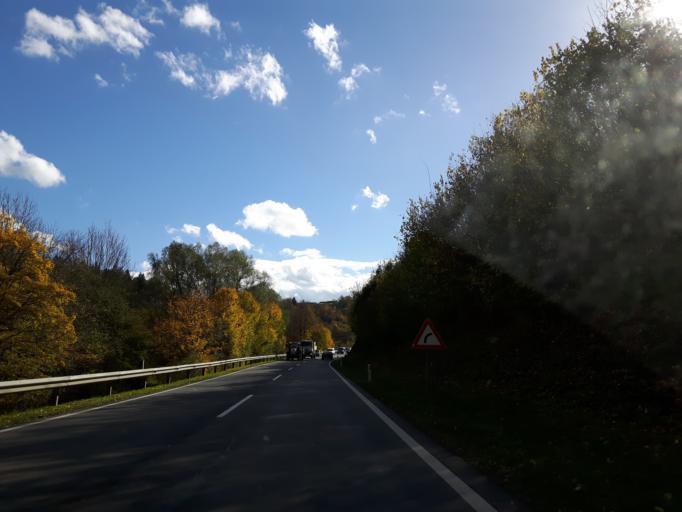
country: AT
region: Styria
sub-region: Politischer Bezirk Leibnitz
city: Seggauberg
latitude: 46.7824
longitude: 15.5176
